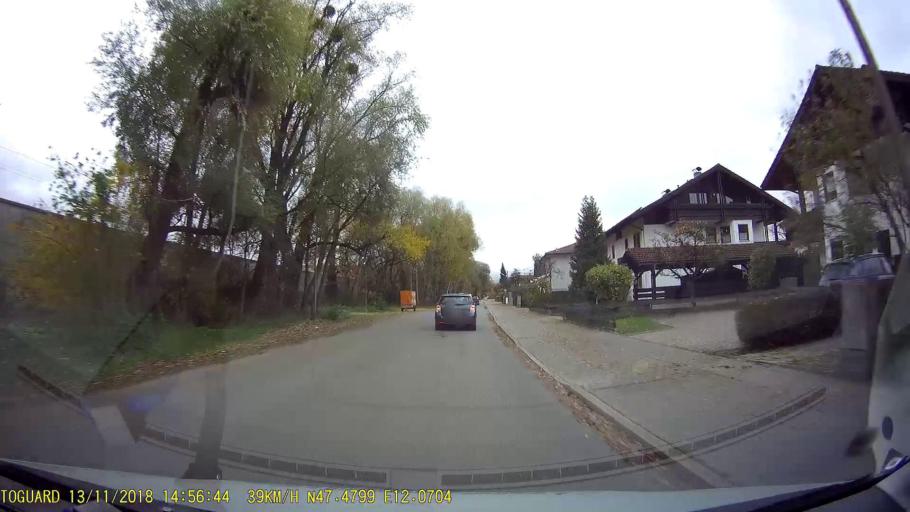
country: DE
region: Bavaria
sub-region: Upper Bavaria
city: Raubling
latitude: 47.7998
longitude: 12.1173
